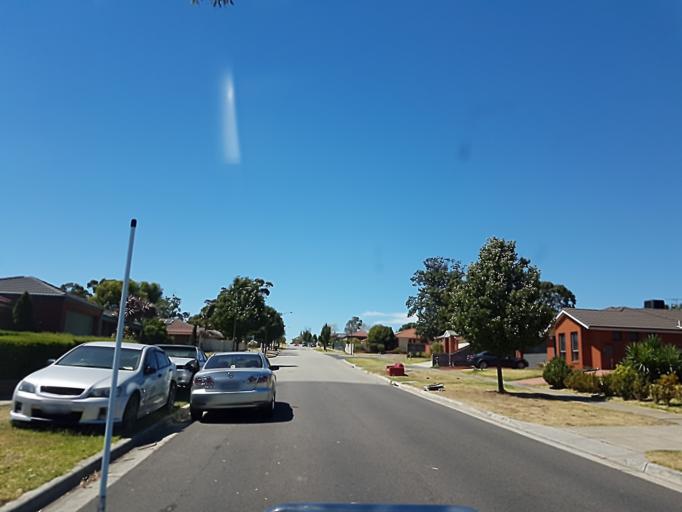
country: AU
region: Victoria
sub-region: Casey
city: Hampton Park
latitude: -38.0416
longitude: 145.2559
